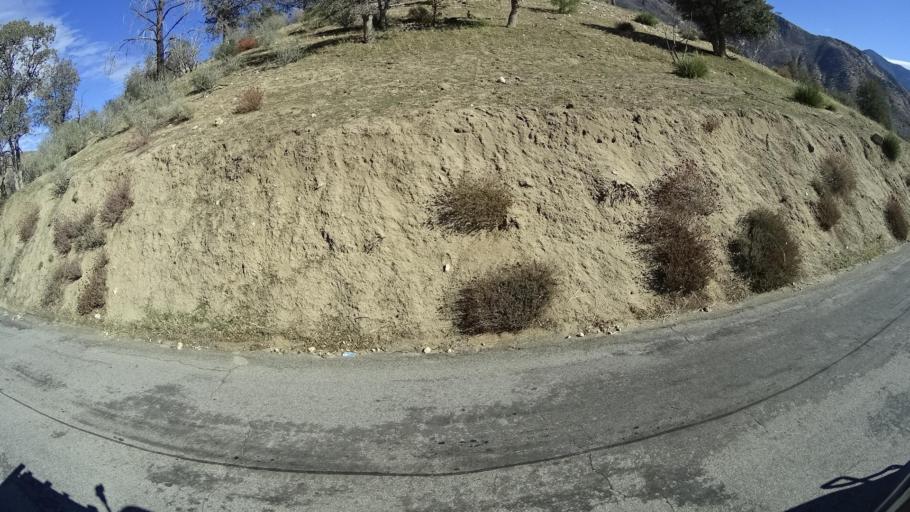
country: US
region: California
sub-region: Kern County
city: Bodfish
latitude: 35.5573
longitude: -118.5102
